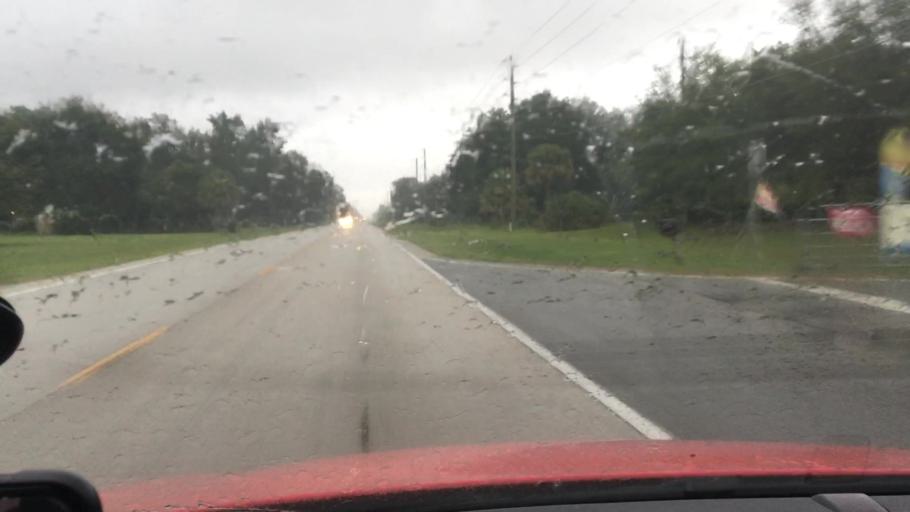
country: US
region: Florida
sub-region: Lake County
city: Mount Dora
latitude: 28.8512
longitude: -81.6289
